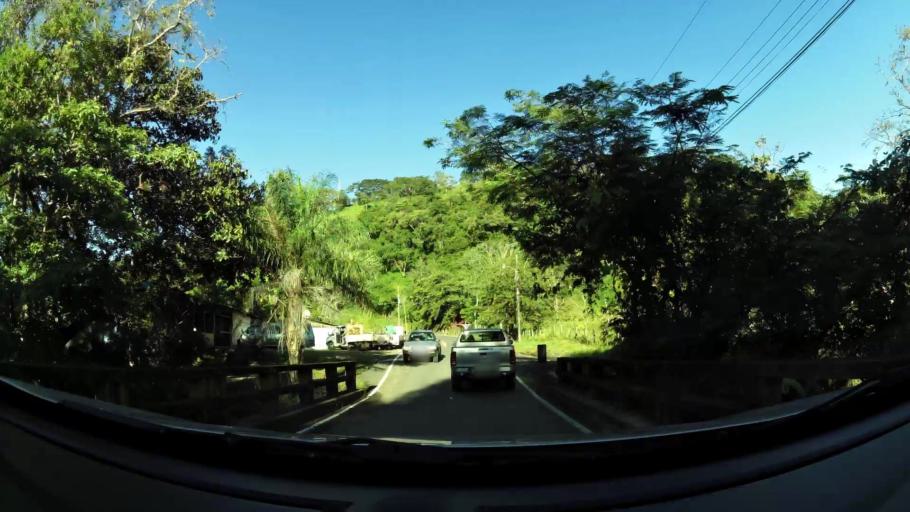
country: CR
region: Guanacaste
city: Juntas
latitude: 10.2168
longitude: -84.8505
